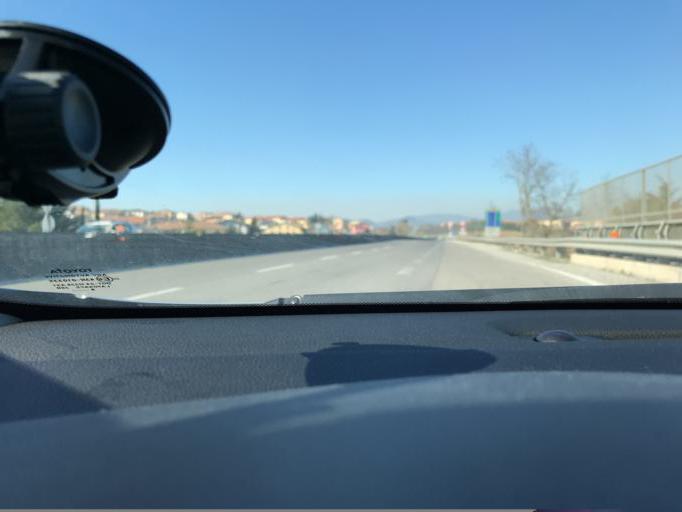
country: IT
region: Umbria
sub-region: Provincia di Perugia
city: Via Lippia
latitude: 43.0840
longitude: 12.4870
